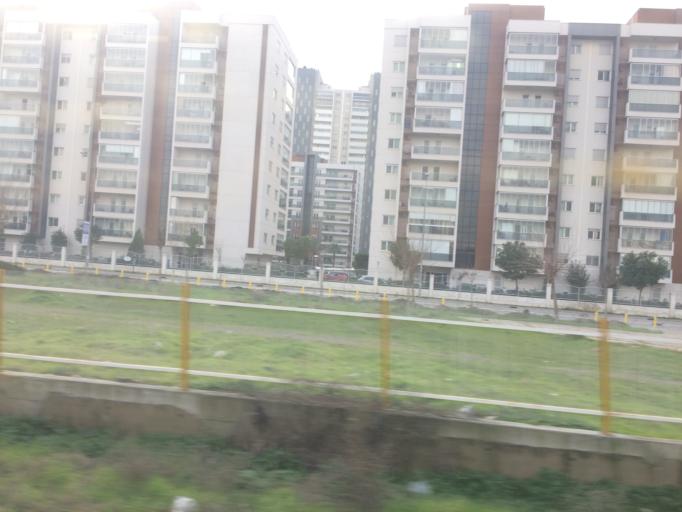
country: TR
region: Izmir
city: Karsiyaka
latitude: 38.4791
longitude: 27.0858
